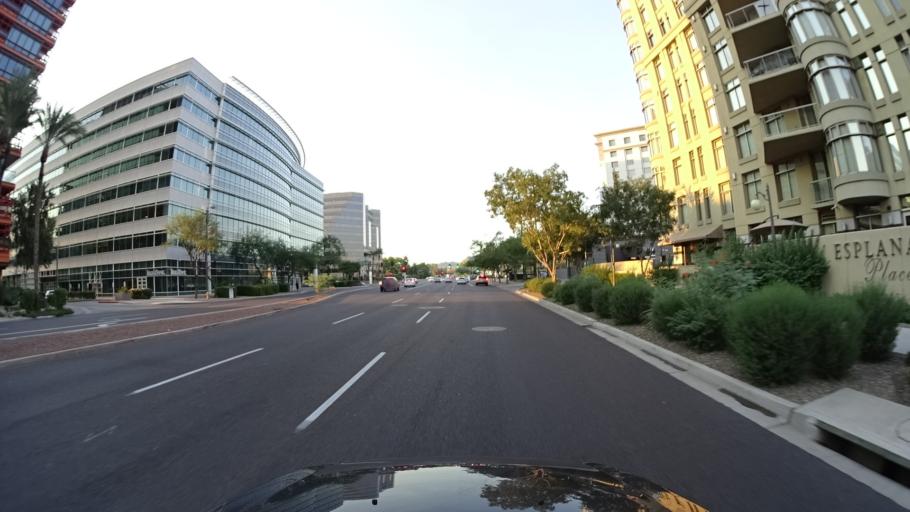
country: US
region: Arizona
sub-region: Maricopa County
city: Phoenix
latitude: 33.5079
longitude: -112.0301
